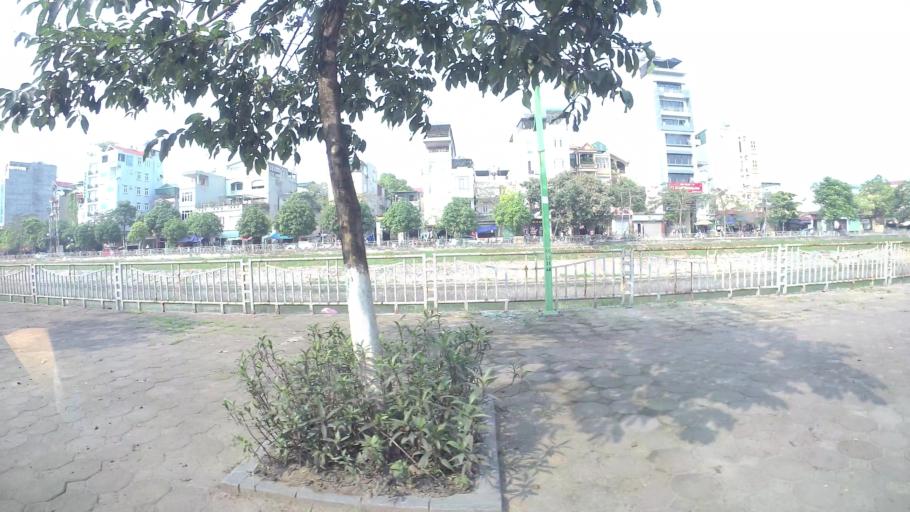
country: VN
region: Ha Noi
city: Thanh Xuan
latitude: 20.9816
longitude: 105.8170
